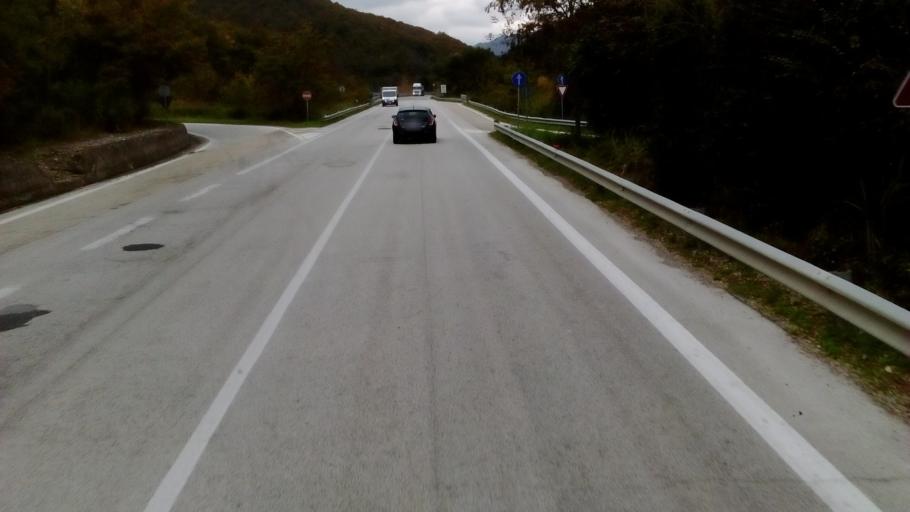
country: IT
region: Molise
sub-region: Provincia di Campobasso
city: Montemitro
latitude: 41.9027
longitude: 14.6441
